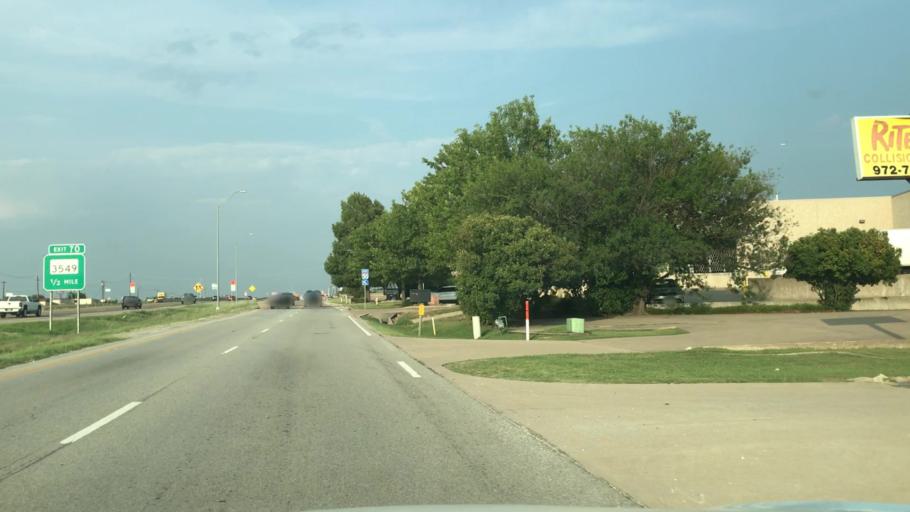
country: US
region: Texas
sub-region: Rockwall County
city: Rockwall
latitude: 32.9138
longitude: -96.4408
